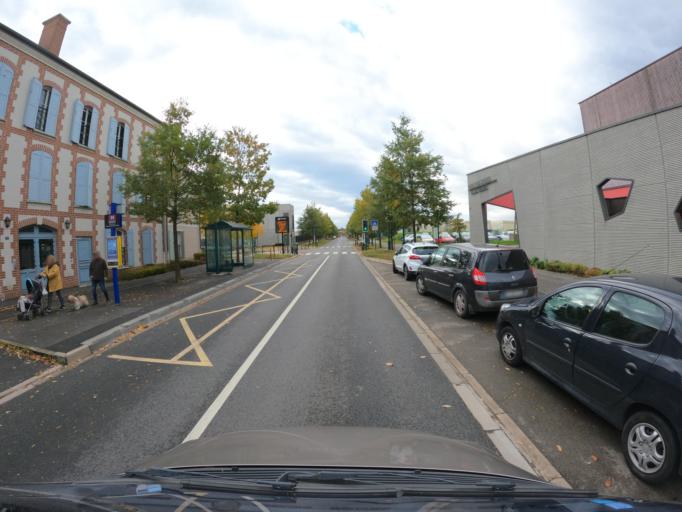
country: FR
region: Ile-de-France
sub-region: Departement de Seine-et-Marne
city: Magny-le-Hongre
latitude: 48.8695
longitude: 2.8120
